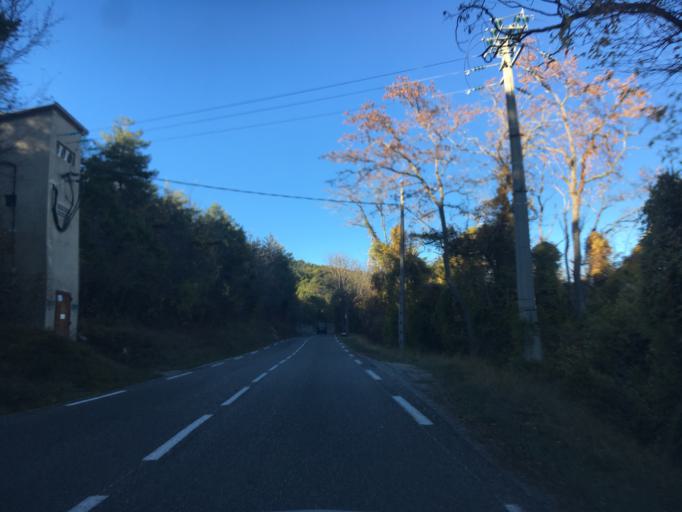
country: FR
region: Provence-Alpes-Cote d'Azur
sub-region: Departement du Var
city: Montferrat
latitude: 43.7150
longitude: 6.5030
